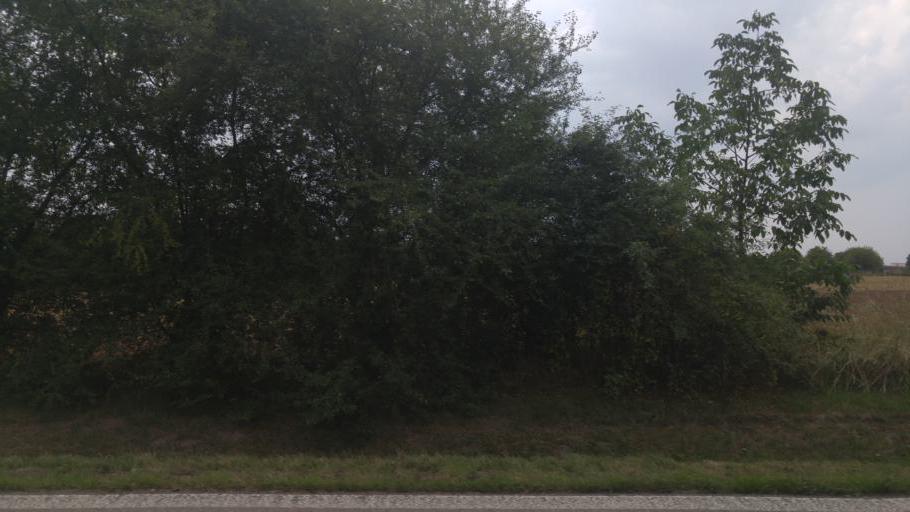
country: CZ
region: Central Bohemia
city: Hostivice
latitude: 50.0886
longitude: 14.3034
